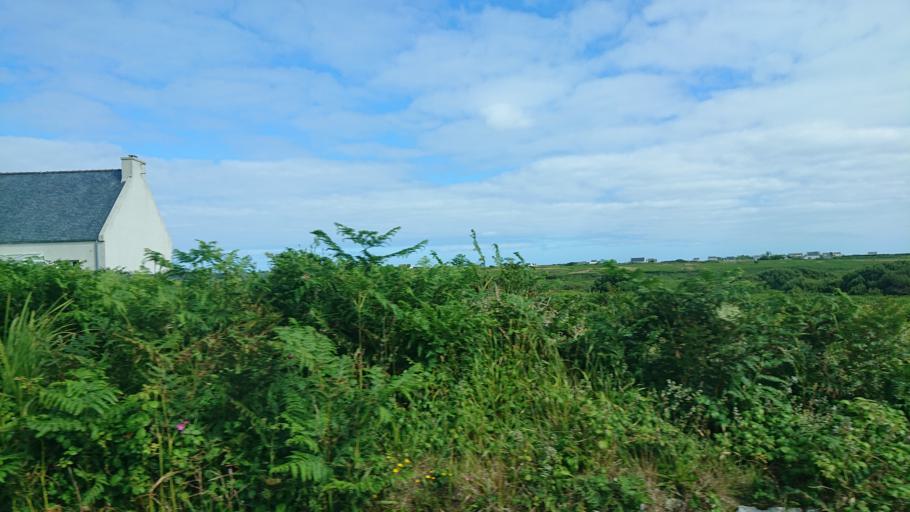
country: FR
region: Brittany
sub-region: Departement du Finistere
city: Porspoder
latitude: 48.4640
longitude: -5.0816
